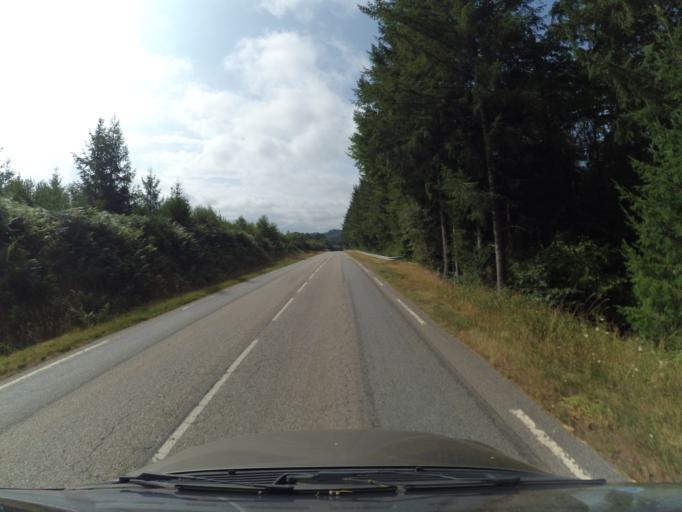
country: FR
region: Limousin
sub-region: Departement de la Correze
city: Meymac
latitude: 45.5914
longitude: 2.1291
